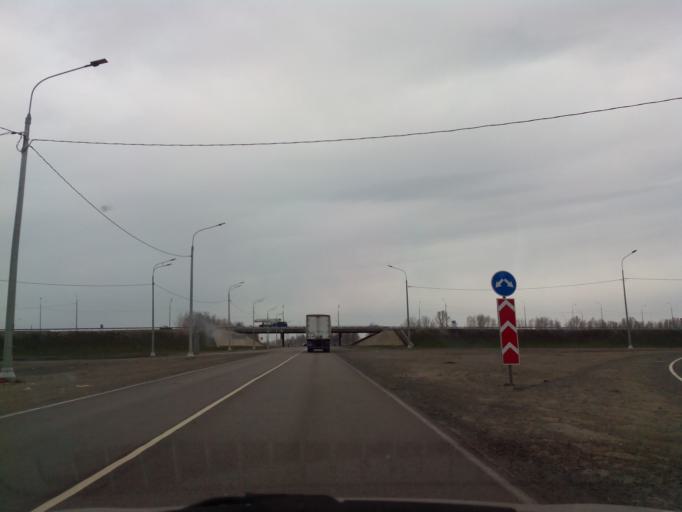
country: RU
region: Tambov
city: Pokrovo-Prigorodnoye
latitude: 52.6589
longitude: 41.3400
